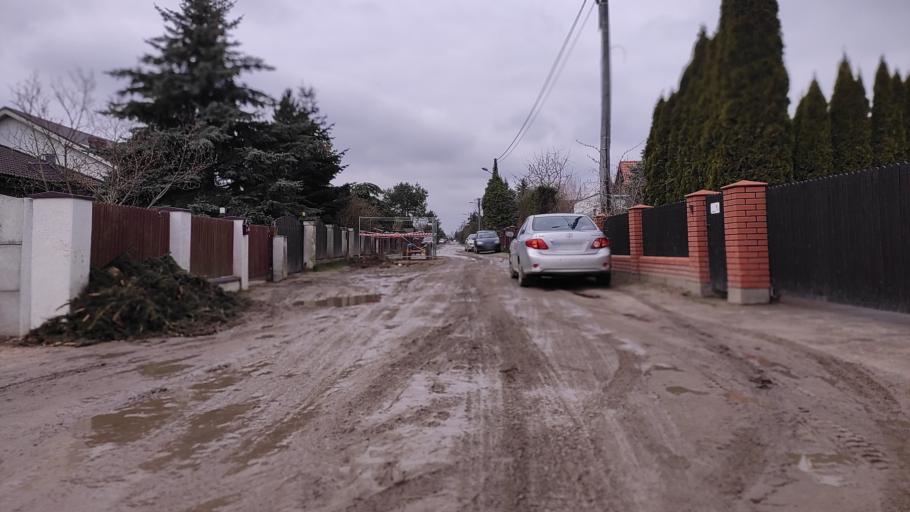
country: PL
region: Greater Poland Voivodeship
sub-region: Powiat poznanski
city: Kostrzyn
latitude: 52.4016
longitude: 17.1706
